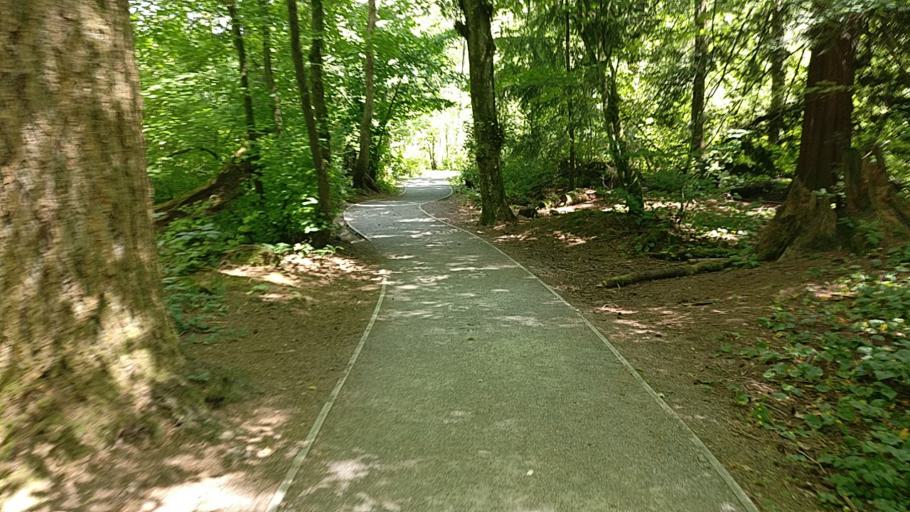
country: CA
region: British Columbia
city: Langley
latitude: 49.0296
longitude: -122.6595
